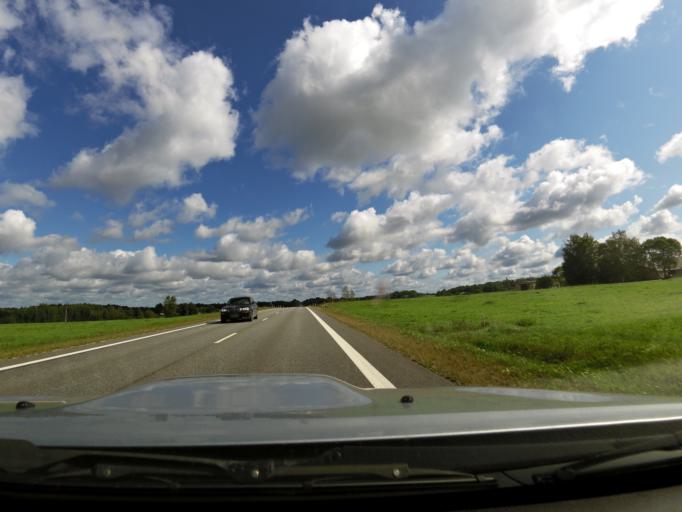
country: LT
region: Utenos apskritis
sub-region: Utena
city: Utena
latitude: 55.5606
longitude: 25.7599
